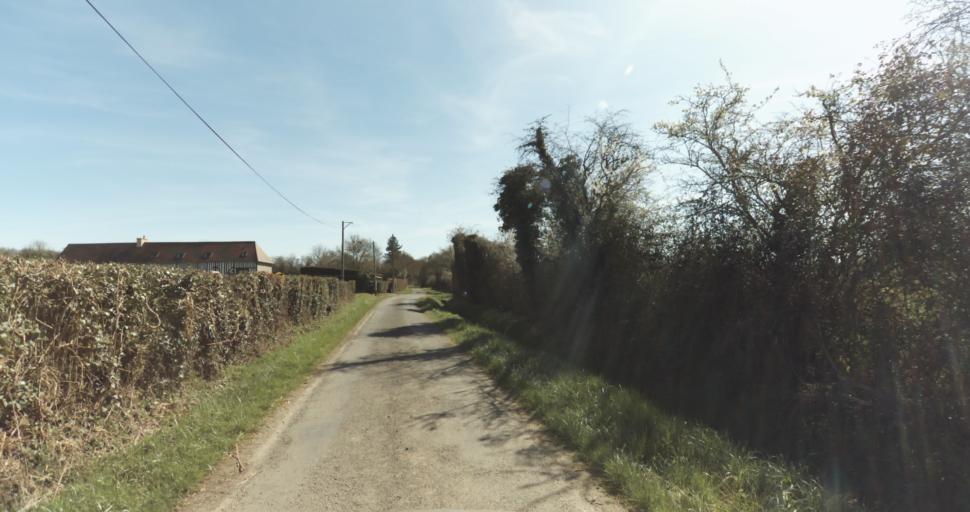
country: FR
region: Lower Normandy
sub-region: Departement du Calvados
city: Saint-Pierre-sur-Dives
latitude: 49.0590
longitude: -0.0260
